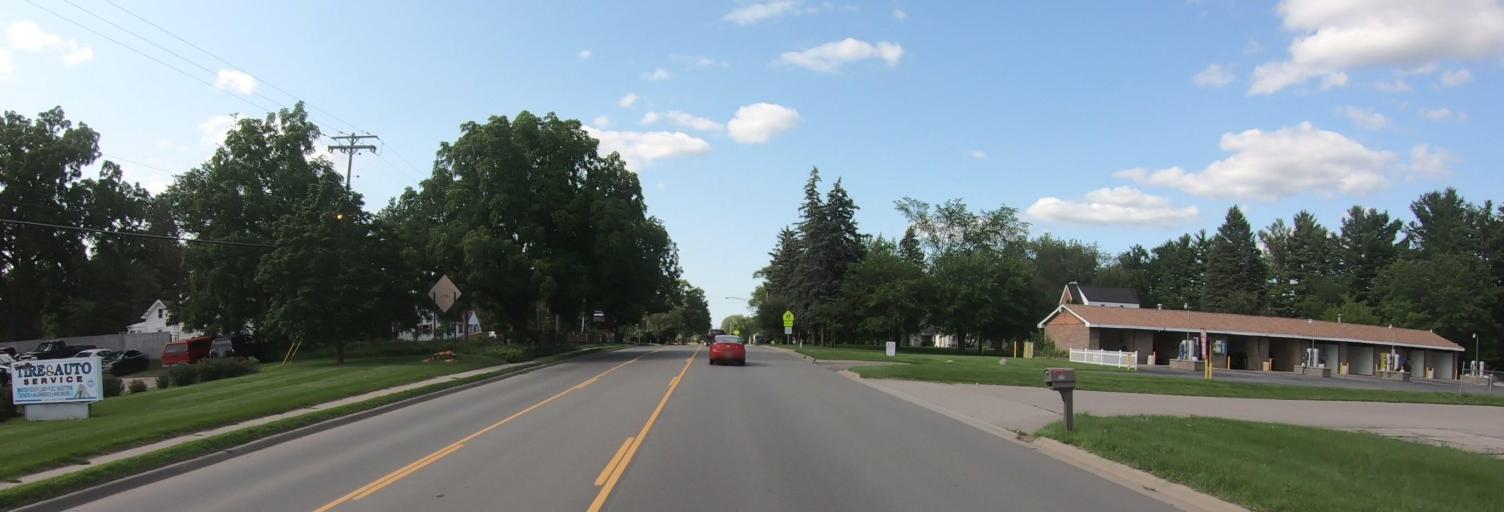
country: US
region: Michigan
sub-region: Oakland County
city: Holly
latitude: 42.8098
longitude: -83.6284
